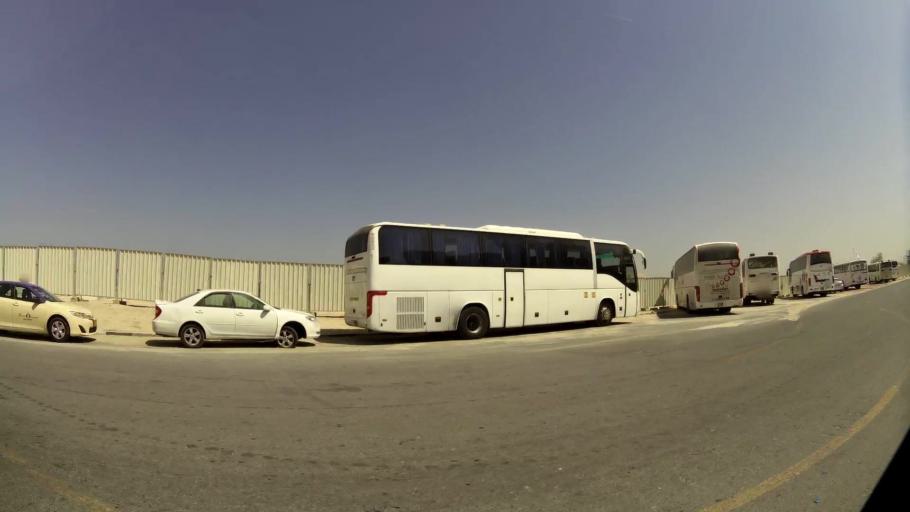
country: AE
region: Ash Shariqah
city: Sharjah
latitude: 25.2207
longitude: 55.2759
